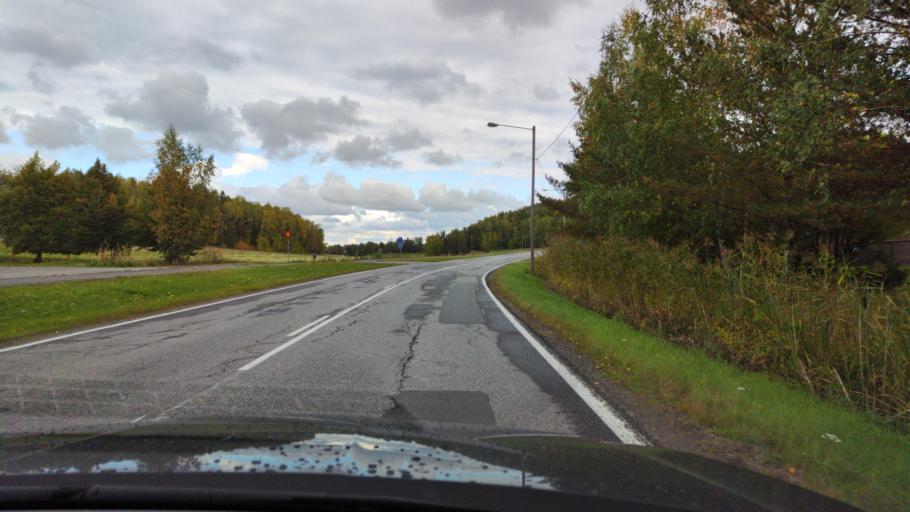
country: FI
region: Varsinais-Suomi
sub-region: Turku
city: Turku
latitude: 60.3614
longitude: 22.1859
